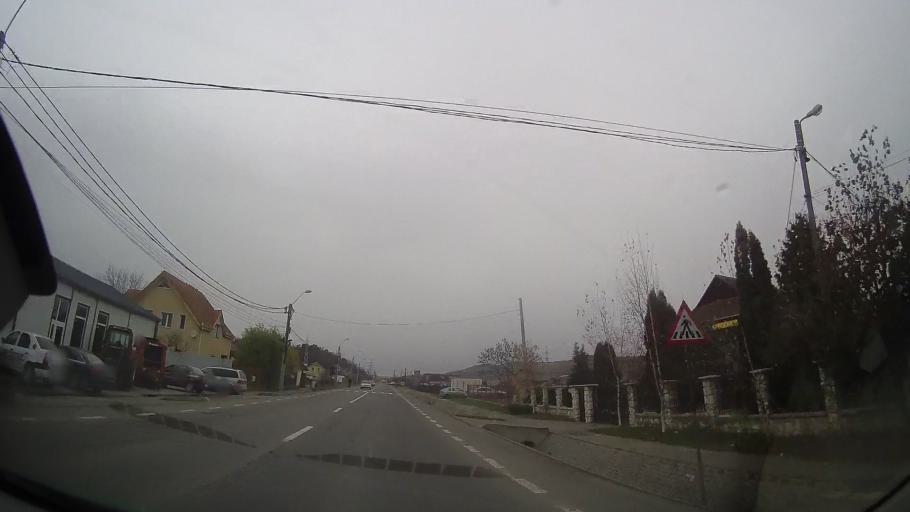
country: RO
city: Remetea
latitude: 46.5901
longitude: 24.5353
